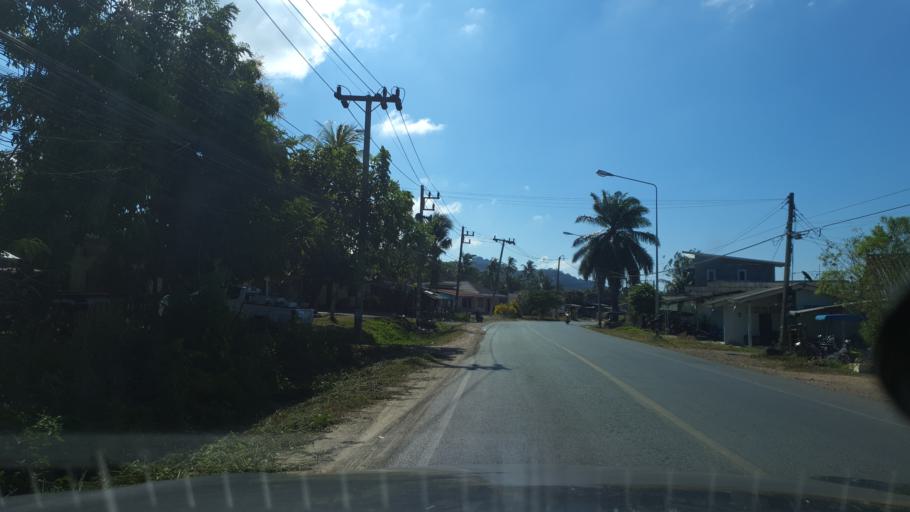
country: TH
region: Phangnga
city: Ban Ao Nang
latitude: 8.0591
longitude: 98.8141
